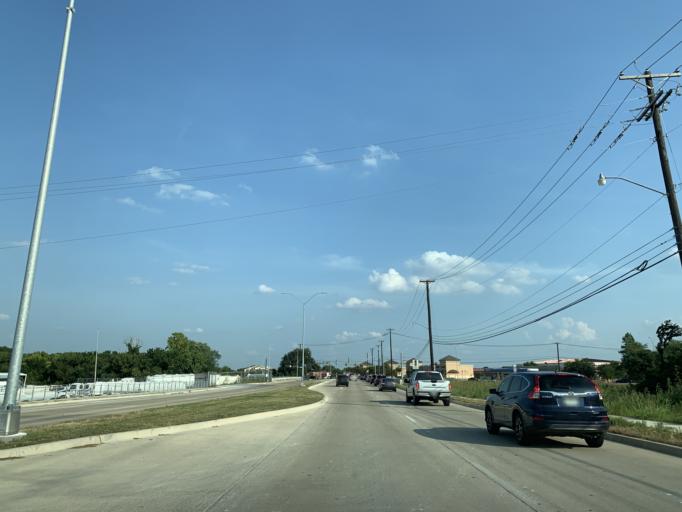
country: US
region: Texas
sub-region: Tarrant County
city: Hurst
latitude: 32.8041
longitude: -97.1851
